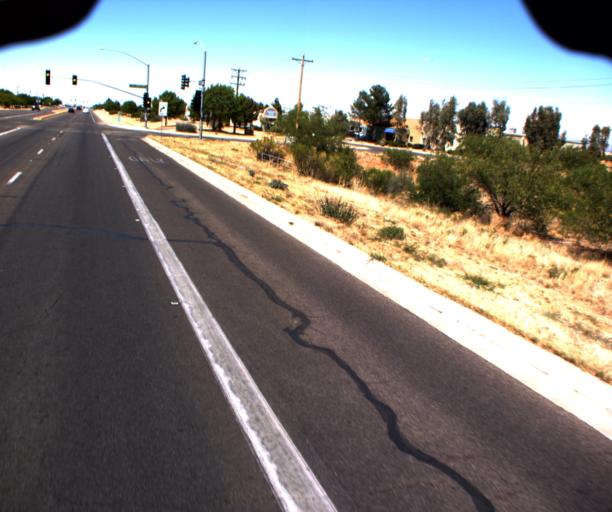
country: US
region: Arizona
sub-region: Cochise County
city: Sierra Vista
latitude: 31.5278
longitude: -110.2573
